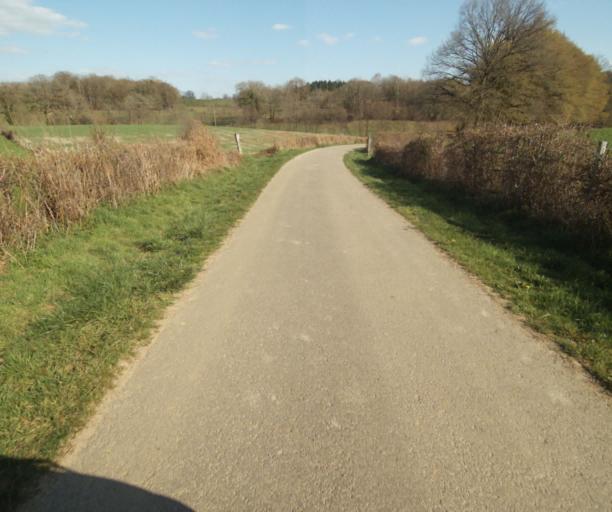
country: FR
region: Limousin
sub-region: Departement de la Correze
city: Saint-Mexant
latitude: 45.3249
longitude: 1.6159
